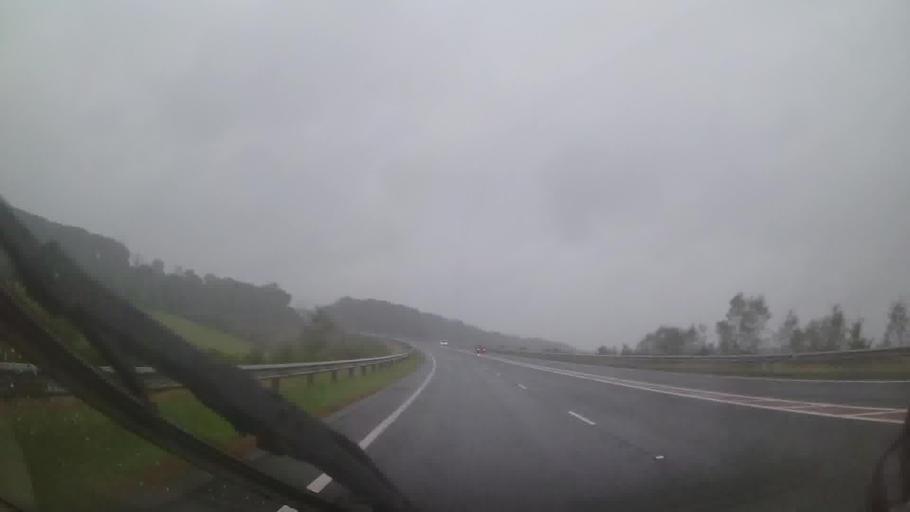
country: GB
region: Wales
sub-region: Carmarthenshire
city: Llanddowror
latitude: 51.8043
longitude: -4.5347
